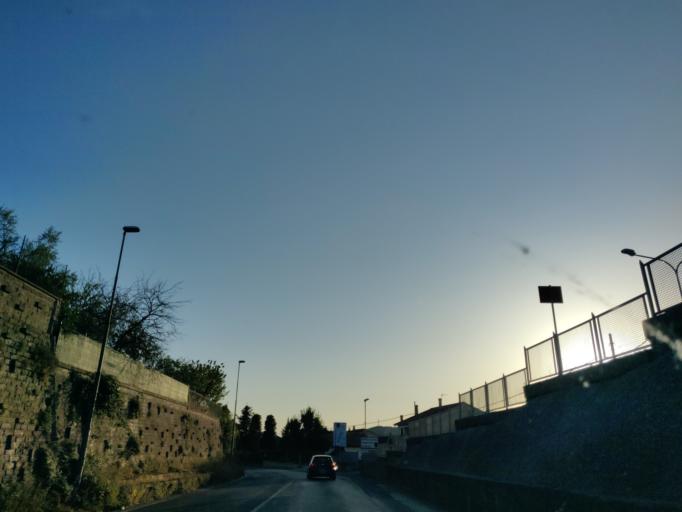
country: IT
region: Latium
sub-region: Provincia di Viterbo
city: Canino
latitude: 42.4609
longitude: 11.7444
